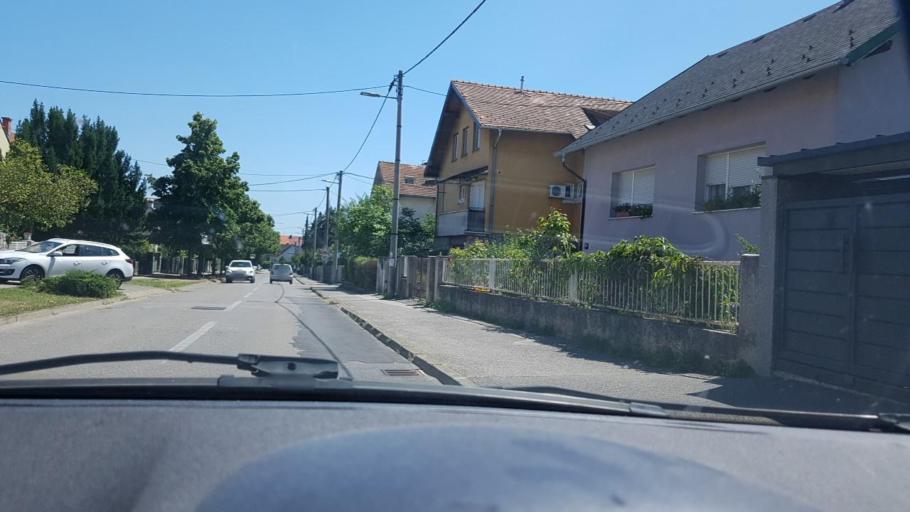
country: HR
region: Grad Zagreb
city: Zagreb
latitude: 45.8322
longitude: 15.9920
